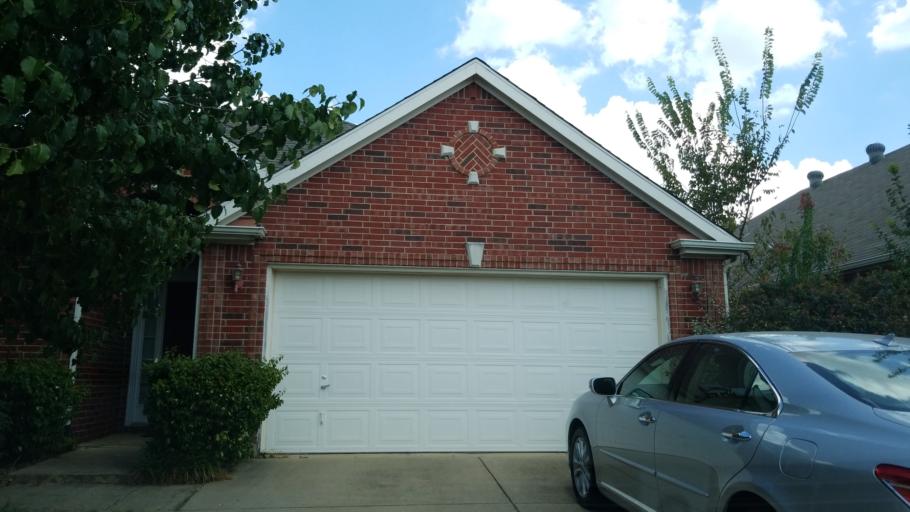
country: US
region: Texas
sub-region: Tarrant County
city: Euless
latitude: 32.8806
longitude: -97.0787
